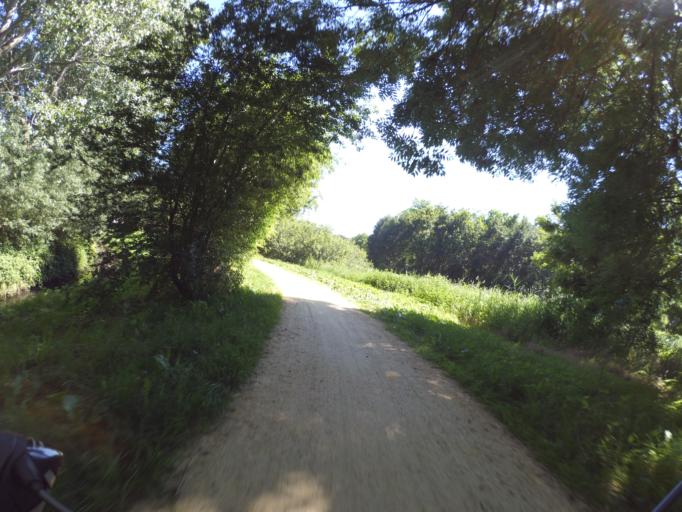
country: NL
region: North Brabant
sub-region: Gemeente Dongen
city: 's Gravenmoer
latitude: 51.6591
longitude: 4.9333
